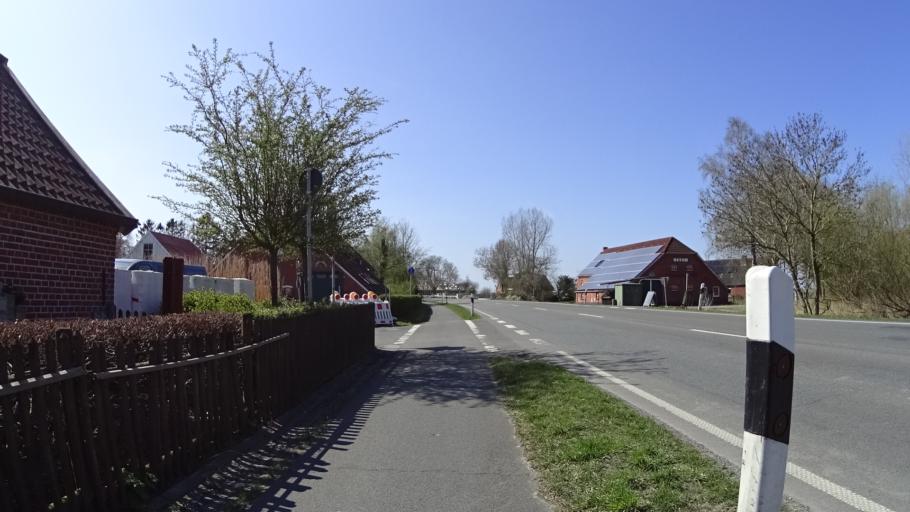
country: DE
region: Lower Saxony
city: Leer
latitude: 53.2096
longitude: 7.4059
